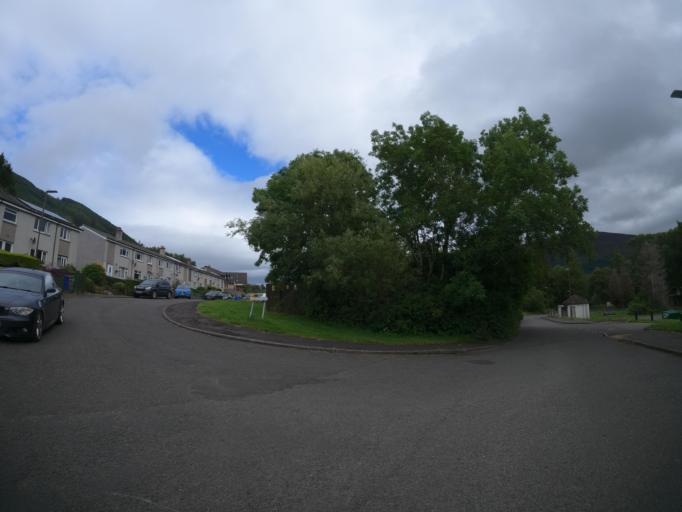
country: GB
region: Scotland
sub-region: Stirling
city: Callander
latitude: 56.3860
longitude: -4.2805
